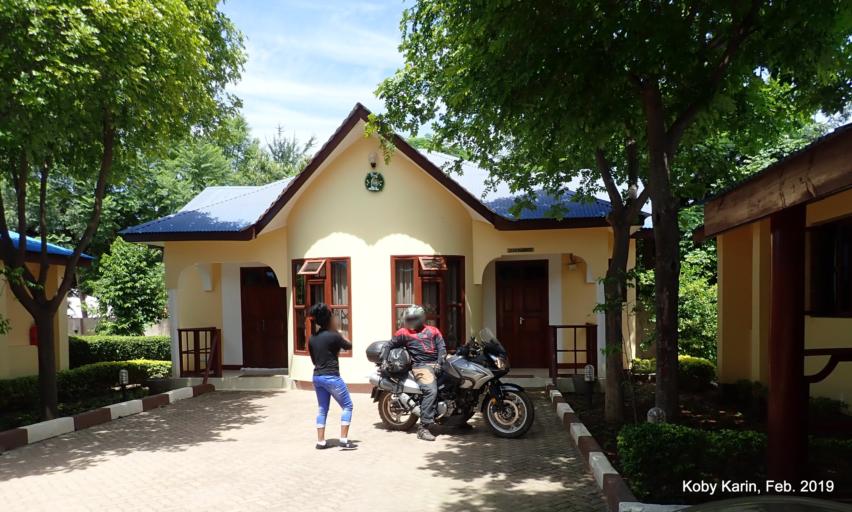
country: TZ
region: Singida
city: Singida
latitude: -4.7994
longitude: 34.7387
